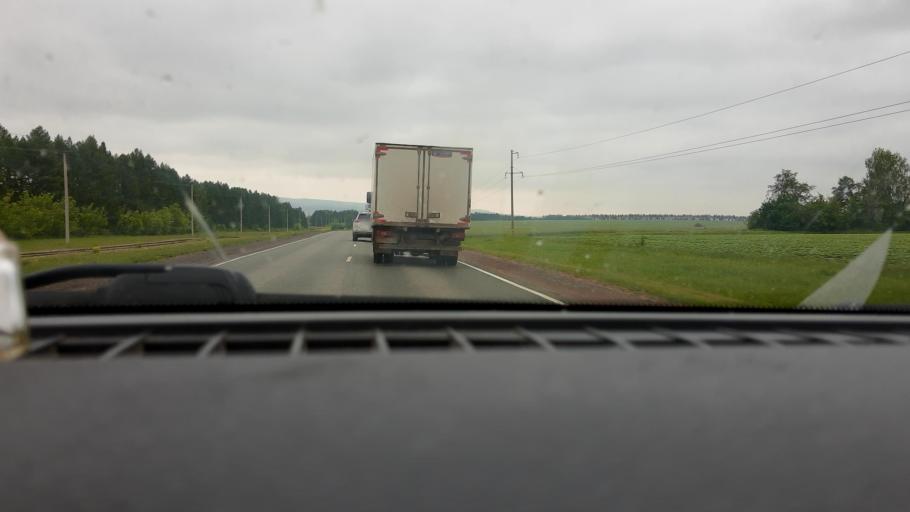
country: RU
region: Bashkortostan
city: Serafimovskiy
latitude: 54.4334
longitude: 53.9789
